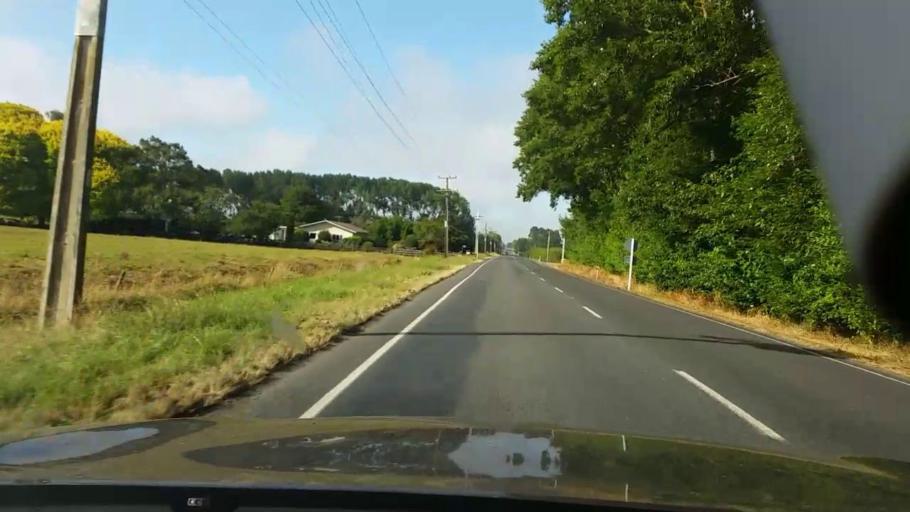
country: NZ
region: Waikato
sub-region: Hamilton City
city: Hamilton
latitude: -37.5996
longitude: 175.3532
